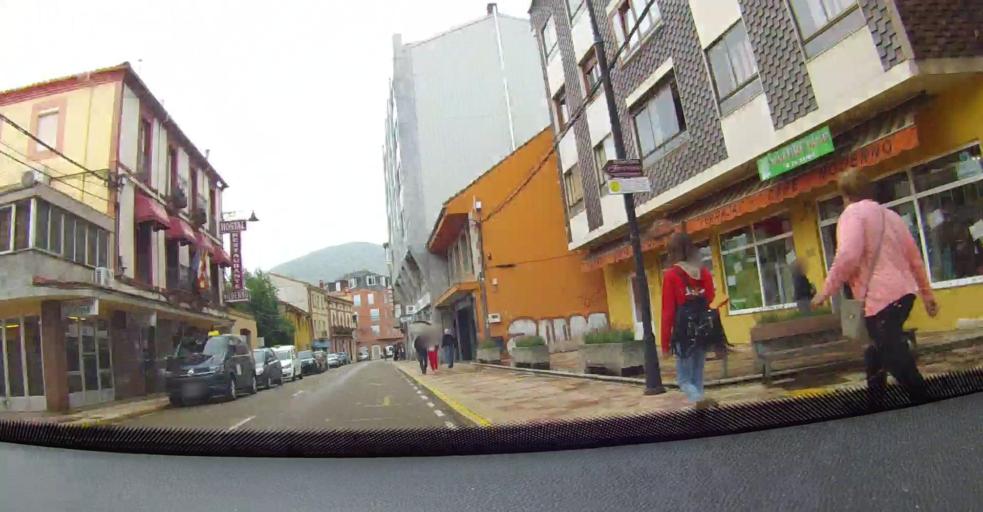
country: ES
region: Castille and Leon
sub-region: Provincia de Leon
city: Cistierna
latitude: 42.8034
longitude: -5.1281
